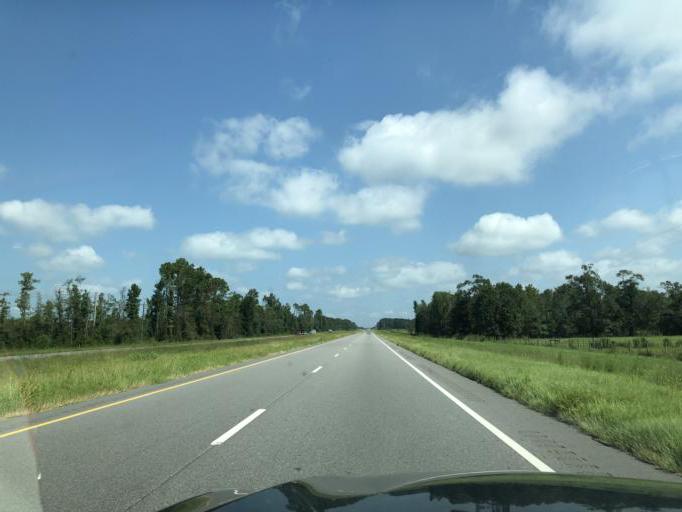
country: US
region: Alabama
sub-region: Houston County
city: Cottonwood
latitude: 31.0273
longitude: -85.4069
